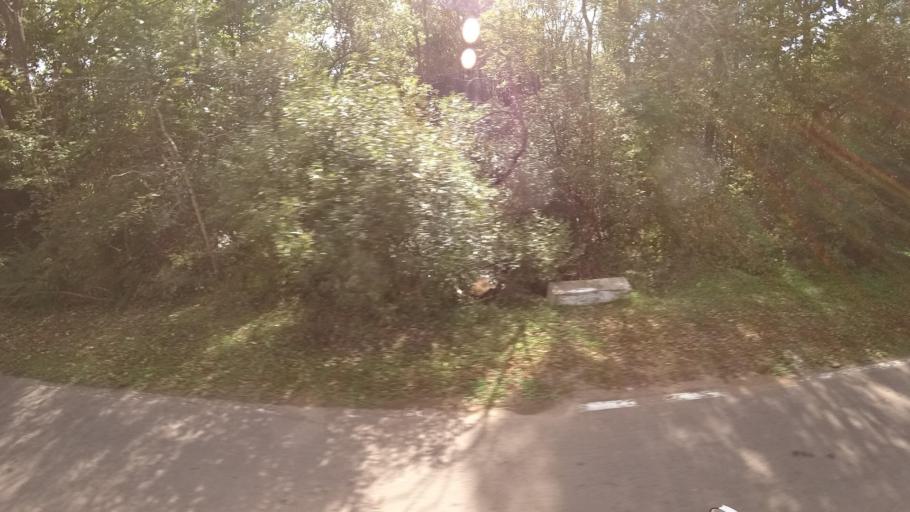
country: RU
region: Primorskiy
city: Yakovlevka
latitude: 44.3954
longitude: 133.6045
